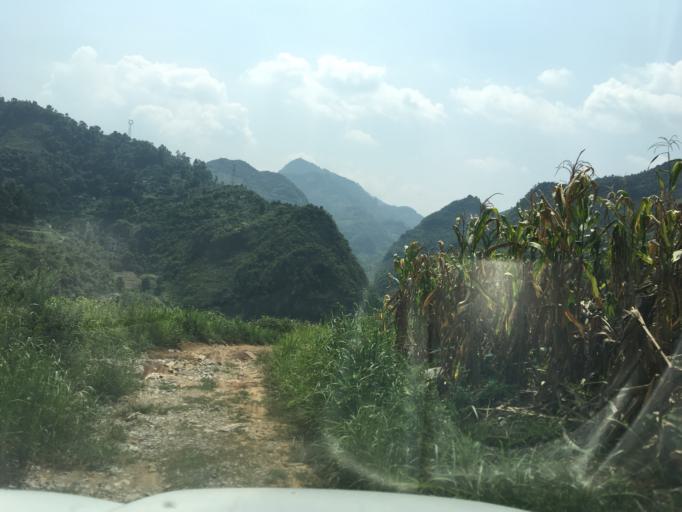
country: CN
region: Guangxi Zhuangzu Zizhiqu
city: Xinzhou
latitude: 24.9942
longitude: 105.7471
